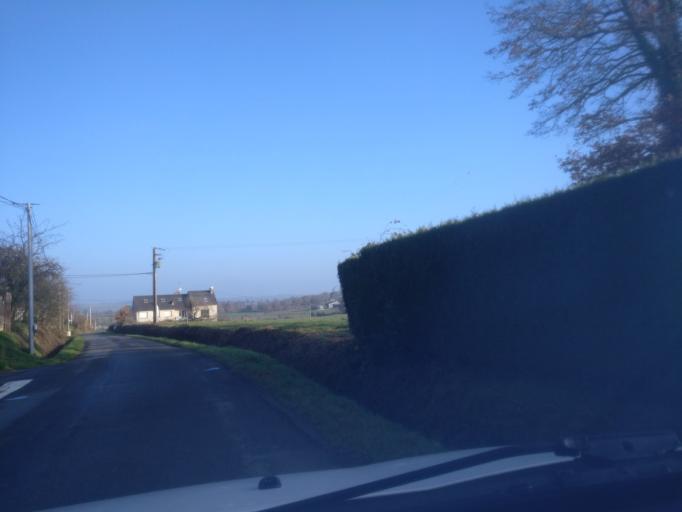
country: FR
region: Brittany
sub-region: Departement d'Ille-et-Vilaine
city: Saint-Jean-sur-Couesnon
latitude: 48.2732
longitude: -1.3664
